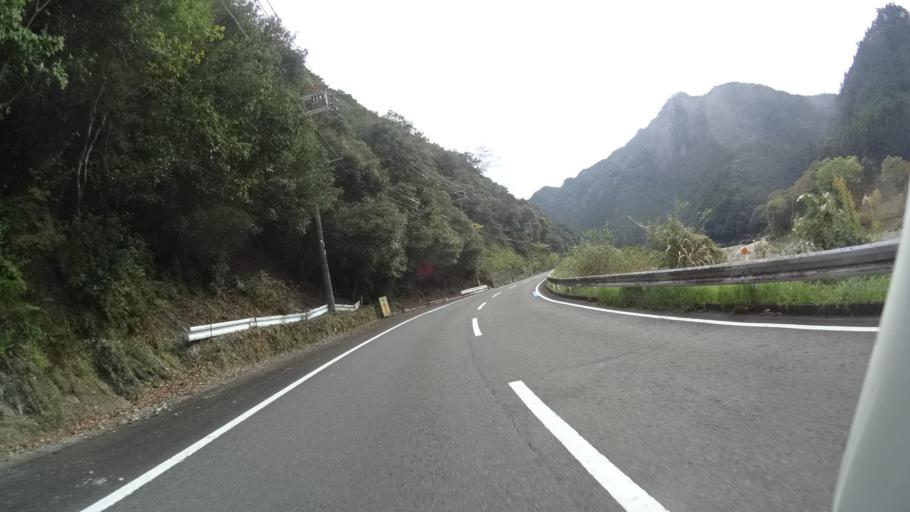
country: JP
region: Wakayama
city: Shingu
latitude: 33.5528
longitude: 135.7020
